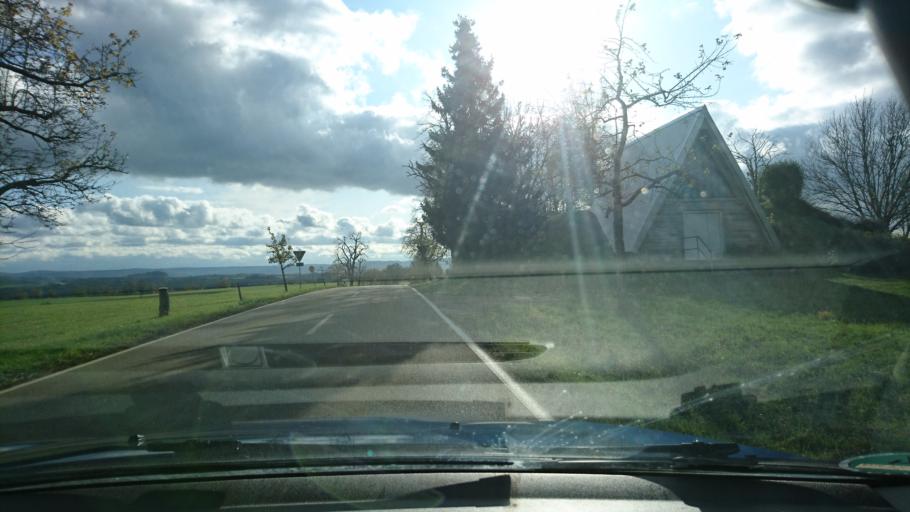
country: DE
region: Baden-Wuerttemberg
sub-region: Regierungsbezirk Stuttgart
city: Abtsgmund
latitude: 48.8909
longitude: 9.9688
